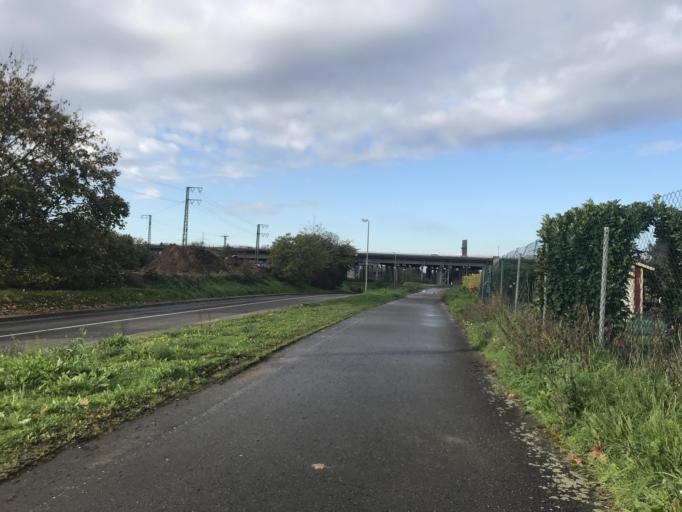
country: DE
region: Hesse
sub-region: Regierungsbezirk Darmstadt
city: Hochheim am Main
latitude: 50.0051
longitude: 8.3469
